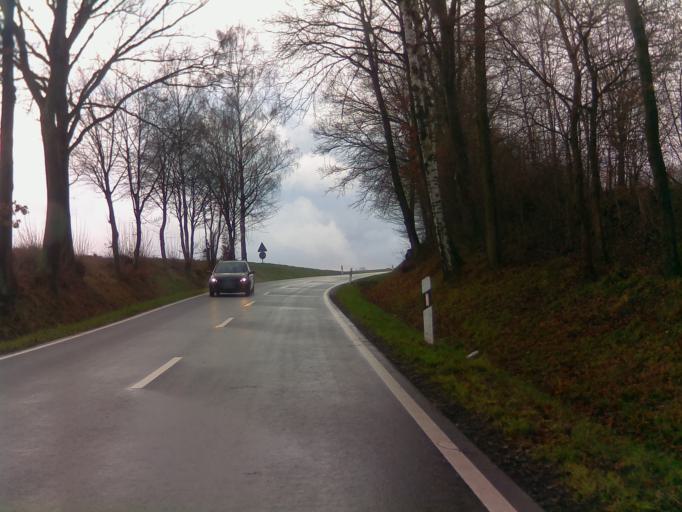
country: DE
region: Hesse
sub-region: Regierungsbezirk Kassel
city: Flieden
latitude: 50.4215
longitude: 9.5937
